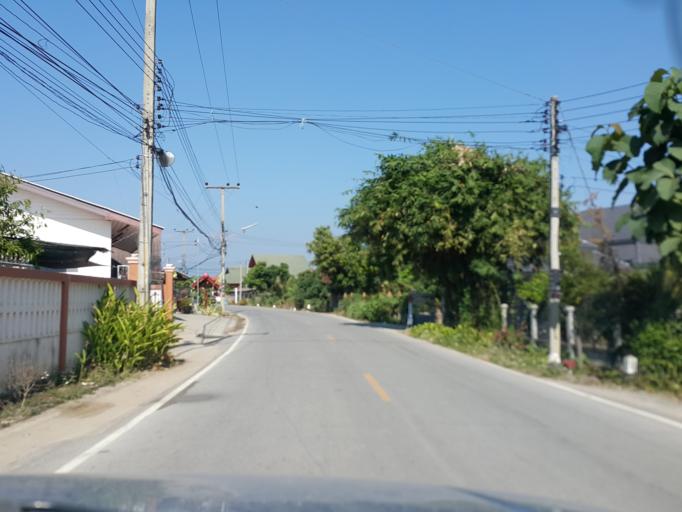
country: TH
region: Chiang Mai
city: Mae Wang
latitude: 18.5983
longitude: 98.8018
